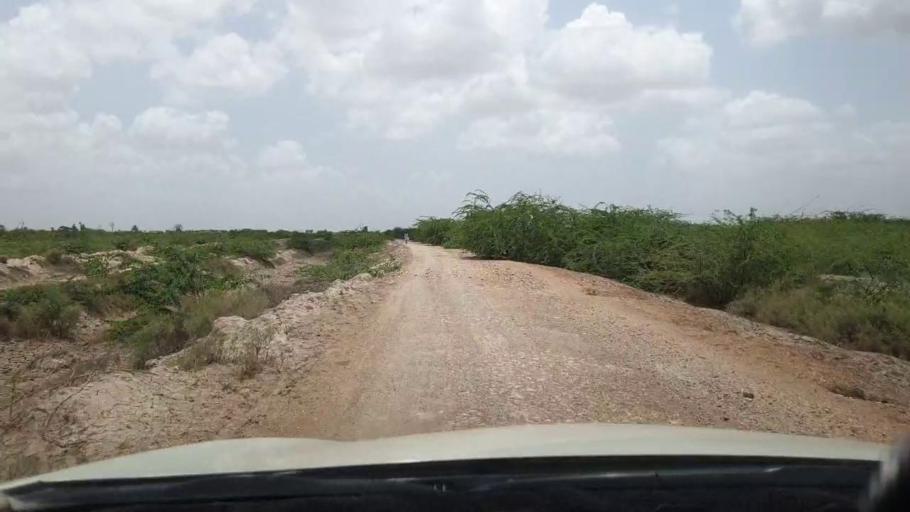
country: PK
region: Sindh
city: Kadhan
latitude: 24.3844
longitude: 68.9318
